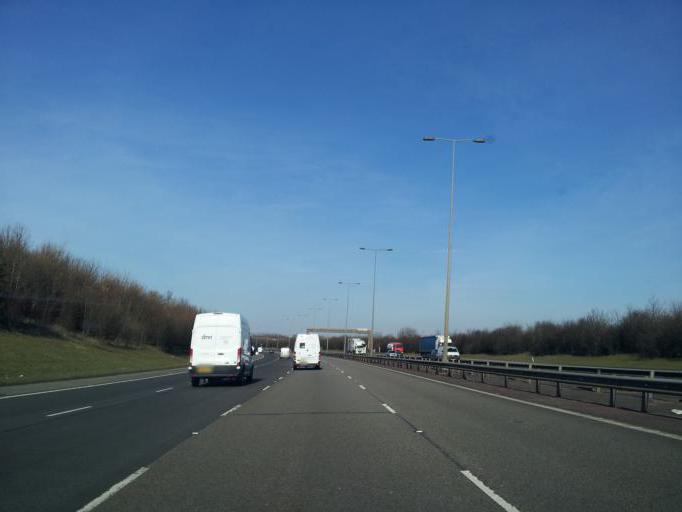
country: GB
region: England
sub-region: Cambridgeshire
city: Stilton
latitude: 52.4855
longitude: -0.2855
